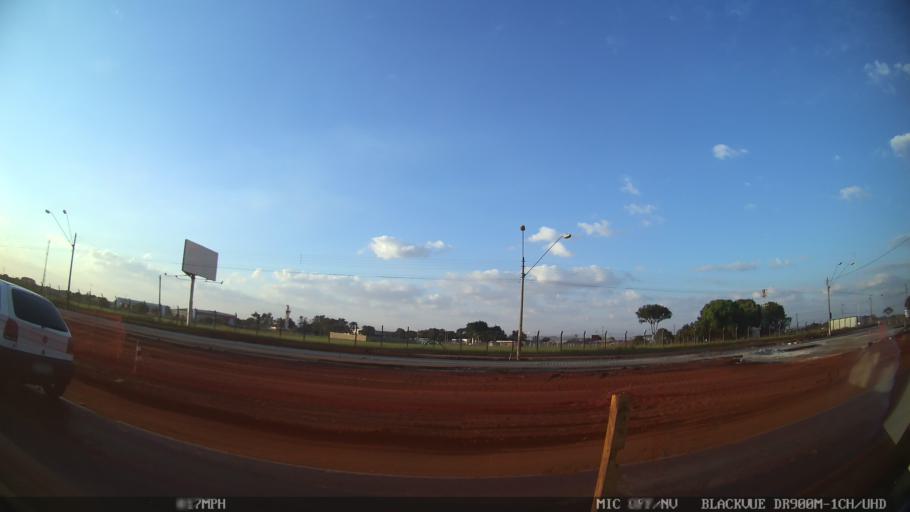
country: BR
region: Sao Paulo
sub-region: Ribeirao Preto
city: Ribeirao Preto
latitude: -21.1430
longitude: -47.7787
